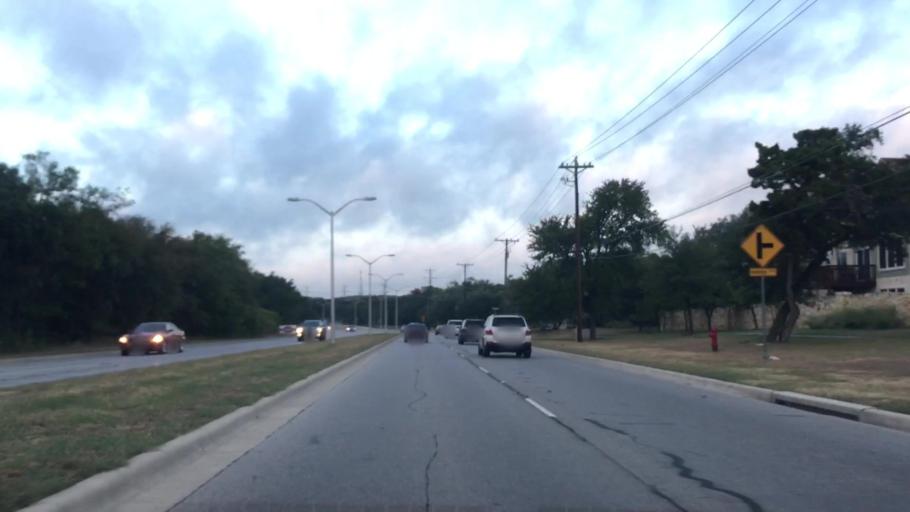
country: US
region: Texas
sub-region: Williamson County
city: Cedar Park
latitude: 30.5064
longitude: -97.7969
